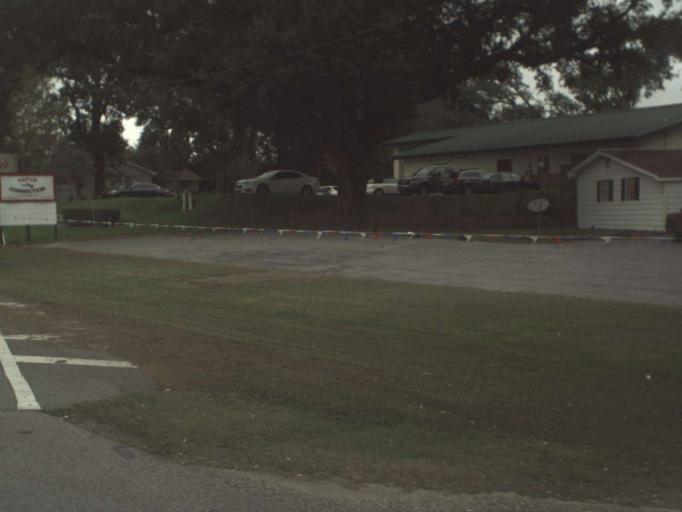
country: US
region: Florida
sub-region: Escambia County
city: Gonzalez
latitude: 30.5660
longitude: -87.2888
